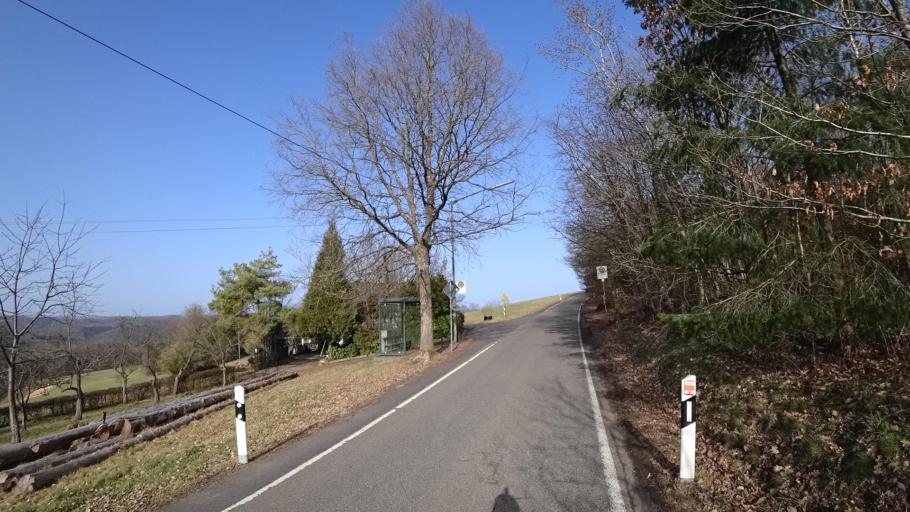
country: DE
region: Rheinland-Pfalz
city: Mittelhof
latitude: 50.7718
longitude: 7.7885
